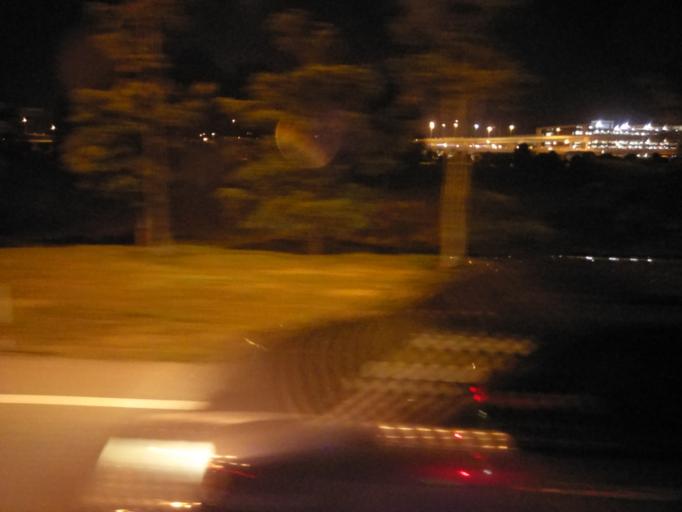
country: MY
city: Sungai Pelek New Village
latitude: 2.7502
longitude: 101.6871
